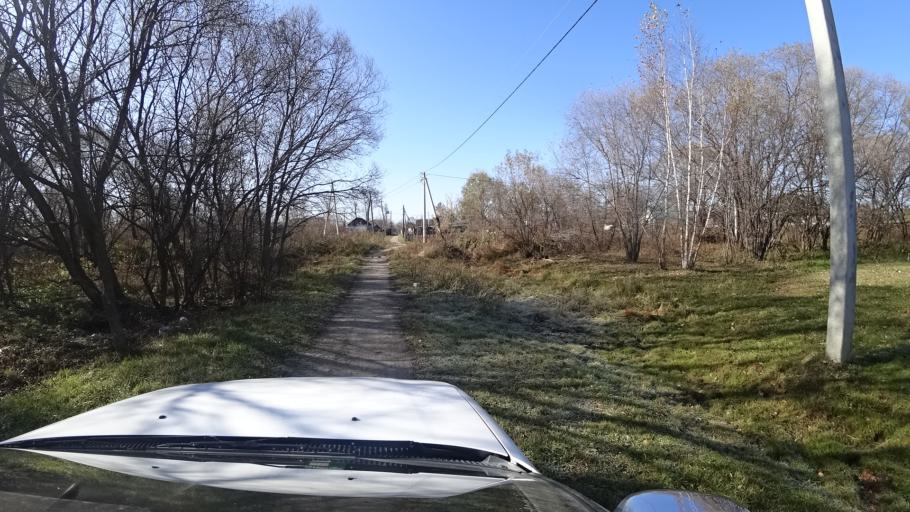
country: RU
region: Primorskiy
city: Dal'nerechensk
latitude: 45.9088
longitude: 133.8013
